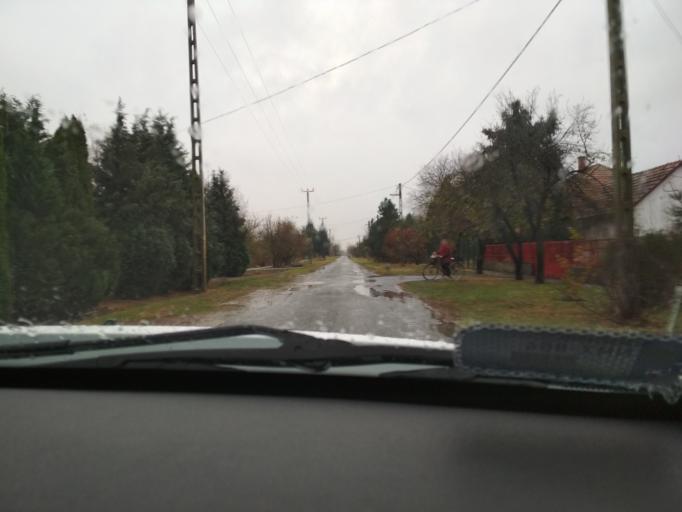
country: HU
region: Csongrad
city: Opusztaszer
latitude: 46.4358
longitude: 20.1389
